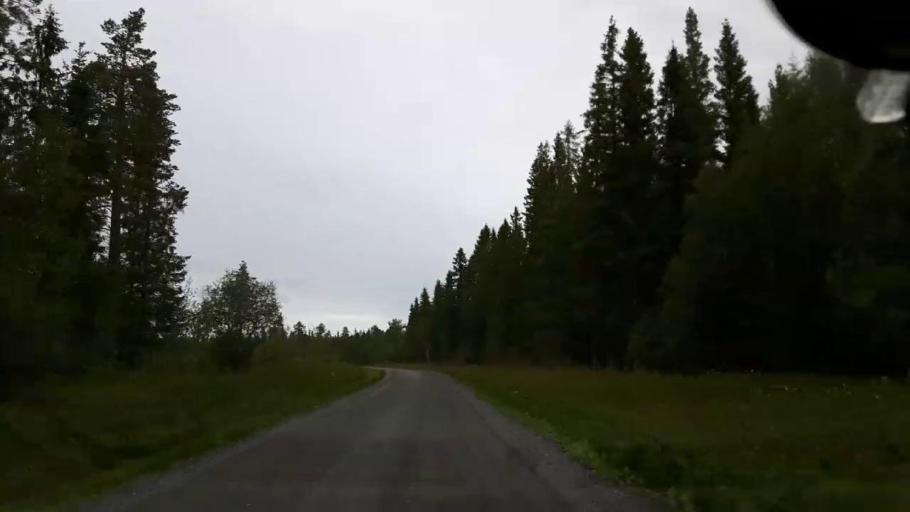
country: SE
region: Jaemtland
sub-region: Krokoms Kommun
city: Krokom
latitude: 63.2863
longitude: 14.3843
